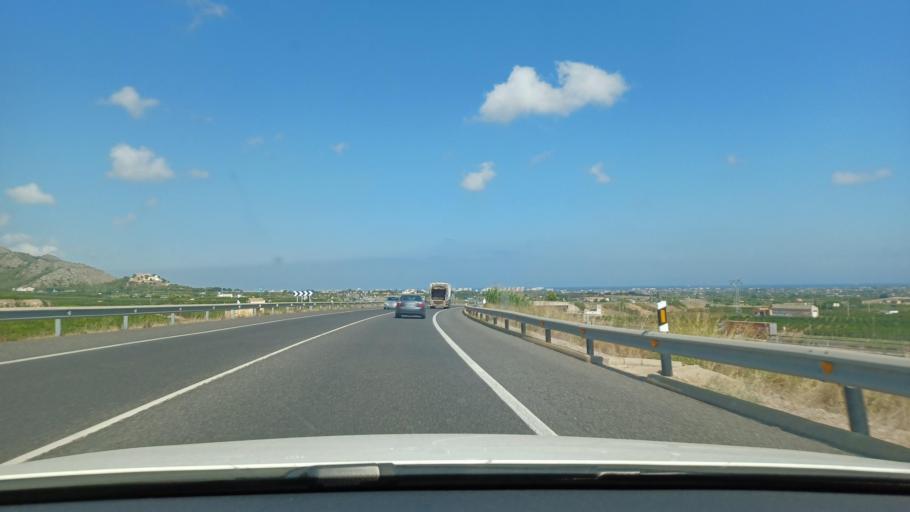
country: ES
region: Valencia
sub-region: Provincia de Castello
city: Borriol
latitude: 40.0285
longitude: -0.0290
